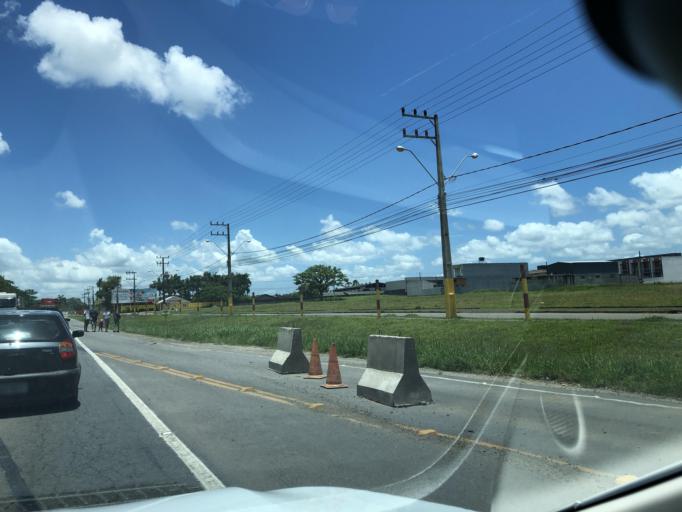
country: BR
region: Santa Catarina
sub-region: Joinville
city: Joinville
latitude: -26.4025
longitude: -48.7441
